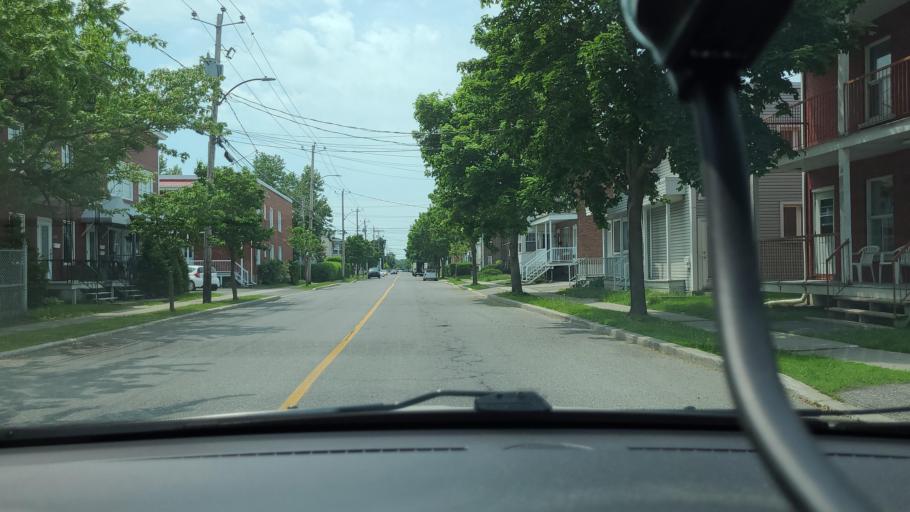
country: CA
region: Quebec
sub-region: Monteregie
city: Saint-Hyacinthe
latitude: 45.6250
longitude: -72.9548
